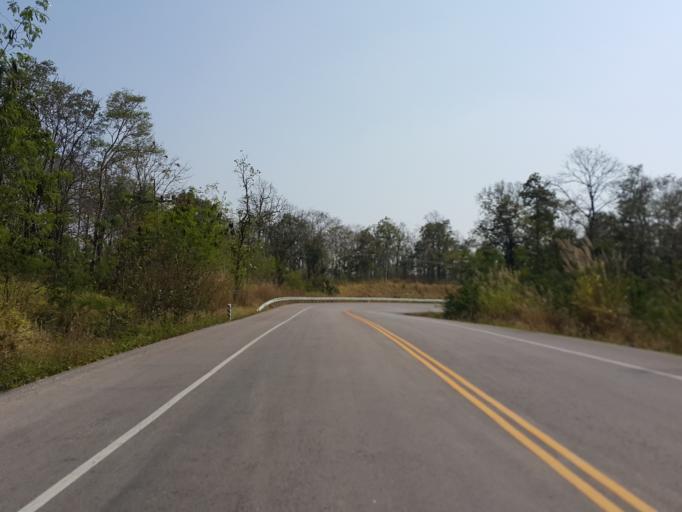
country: TH
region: Lampang
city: Mueang Pan
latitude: 18.8778
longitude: 99.6012
